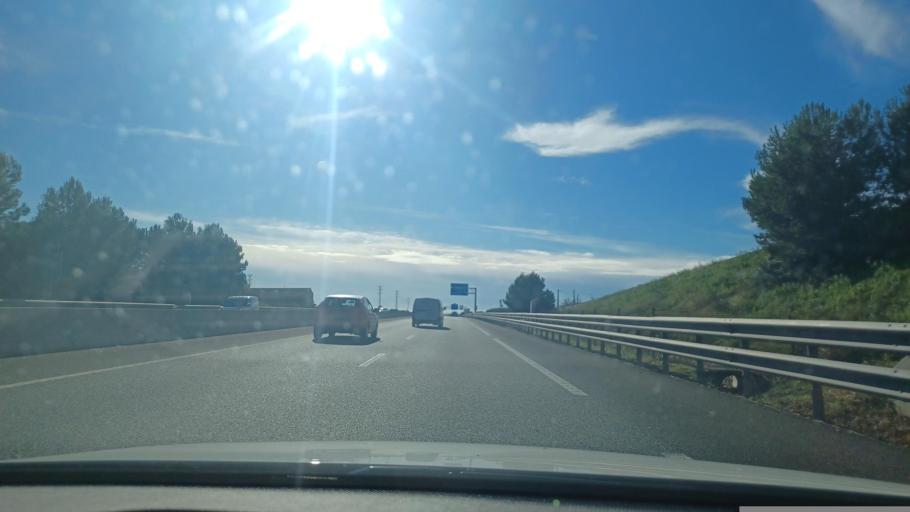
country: ES
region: Catalonia
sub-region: Provincia de Tarragona
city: La Selva
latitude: 41.1912
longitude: 1.1389
